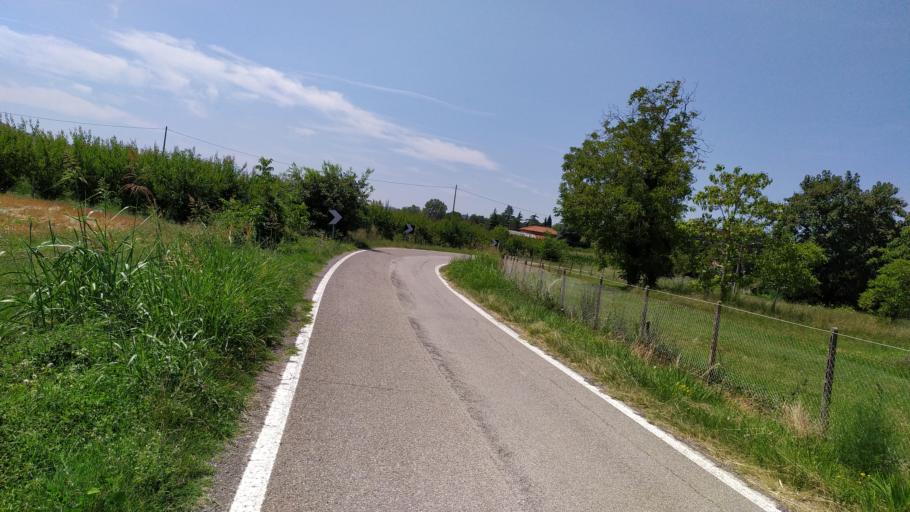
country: IT
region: Emilia-Romagna
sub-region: Forli-Cesena
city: Castrocaro Terme e Terra del Sole
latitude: 44.2008
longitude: 11.9866
